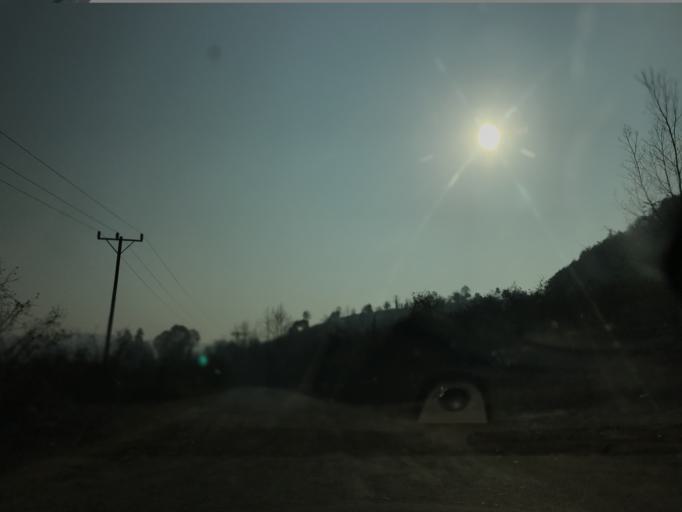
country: TR
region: Duzce
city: Cumayeri
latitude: 40.9139
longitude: 30.9383
